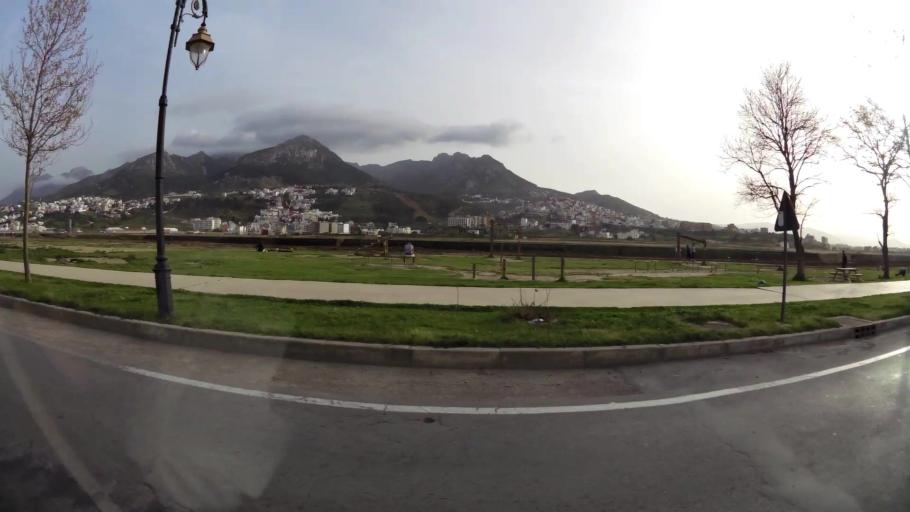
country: MA
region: Tanger-Tetouan
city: Tetouan
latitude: 35.5635
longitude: -5.3771
